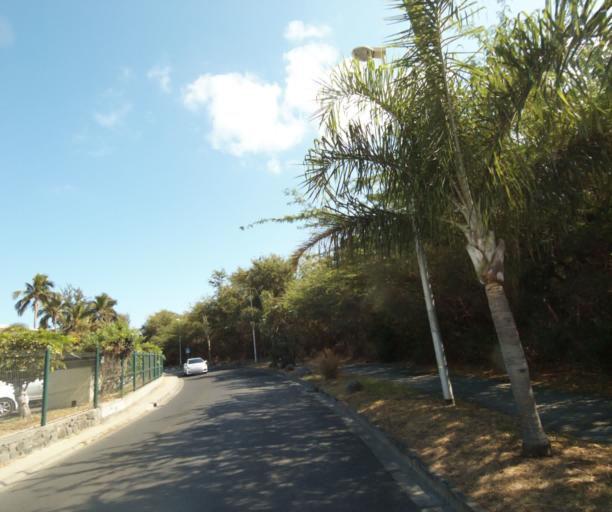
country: RE
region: Reunion
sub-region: Reunion
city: Saint-Paul
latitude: -21.0662
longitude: 55.2228
